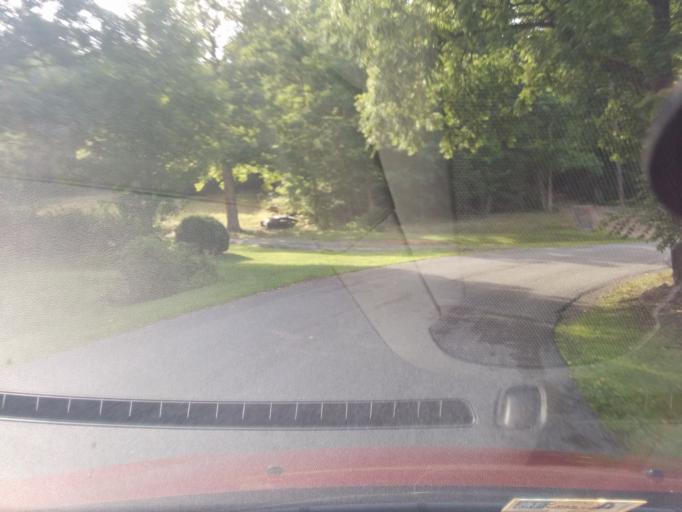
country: US
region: Virginia
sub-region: City of Lexington
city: Lexington
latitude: 37.7749
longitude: -79.4908
